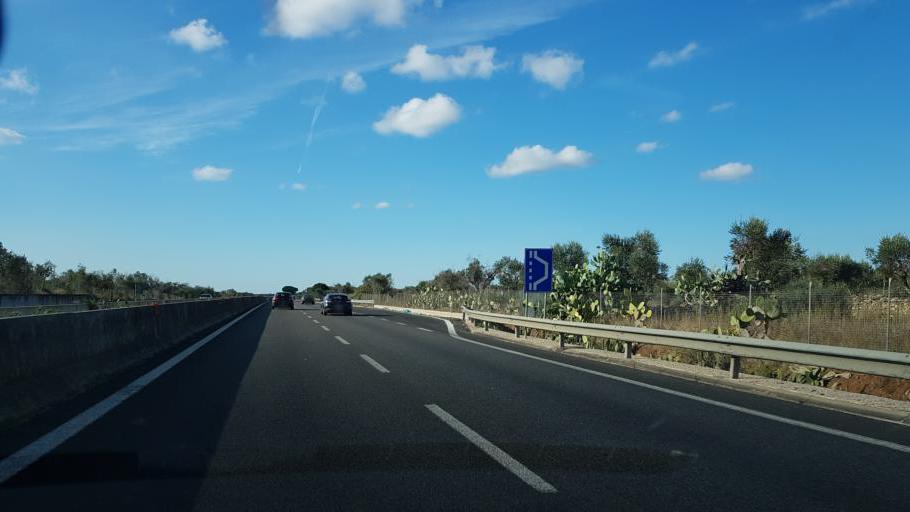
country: IT
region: Apulia
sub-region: Provincia di Lecce
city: Squinzano
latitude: 40.4468
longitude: 18.0726
